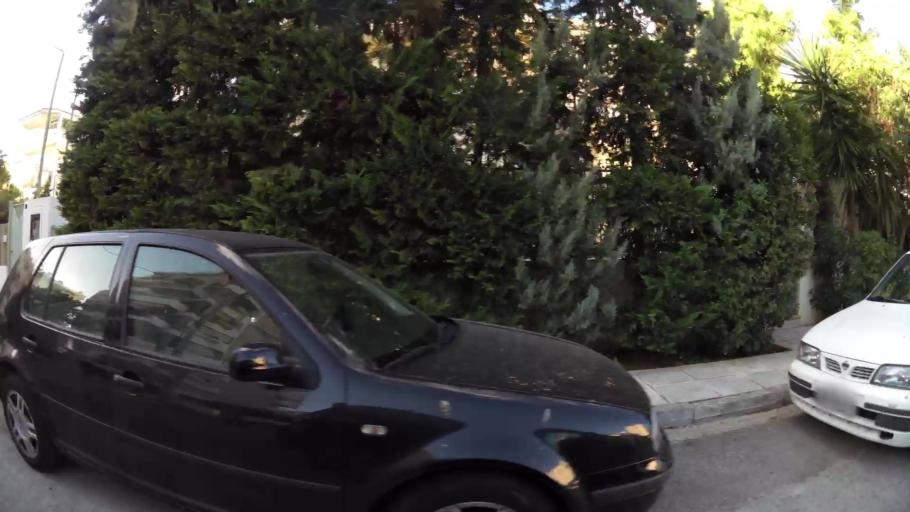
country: GR
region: Attica
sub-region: Nomarchia Athinas
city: Elliniko
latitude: 37.8821
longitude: 23.7472
